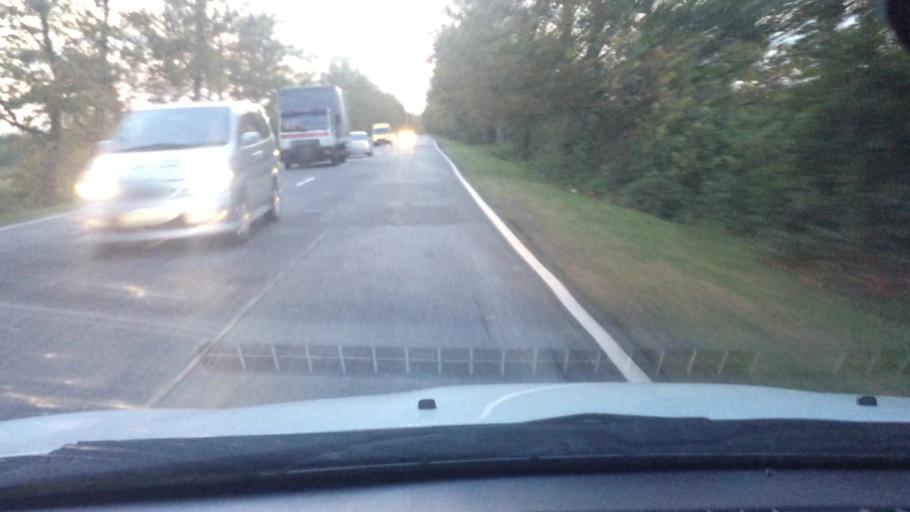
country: GE
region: Guria
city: Urek'i
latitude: 42.0173
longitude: 41.7670
